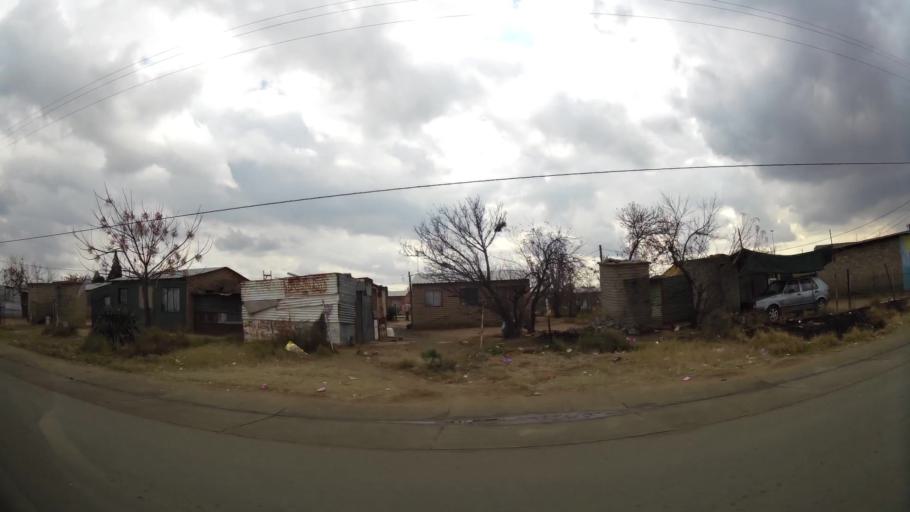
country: ZA
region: Orange Free State
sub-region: Fezile Dabi District Municipality
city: Sasolburg
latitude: -26.8524
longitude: 27.8739
